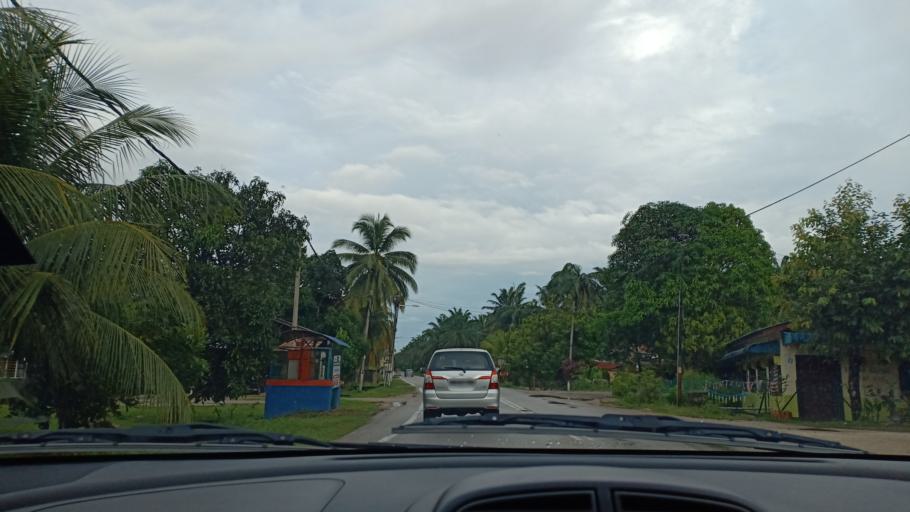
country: MY
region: Penang
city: Tasek Glugor
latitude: 5.4481
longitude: 100.4823
